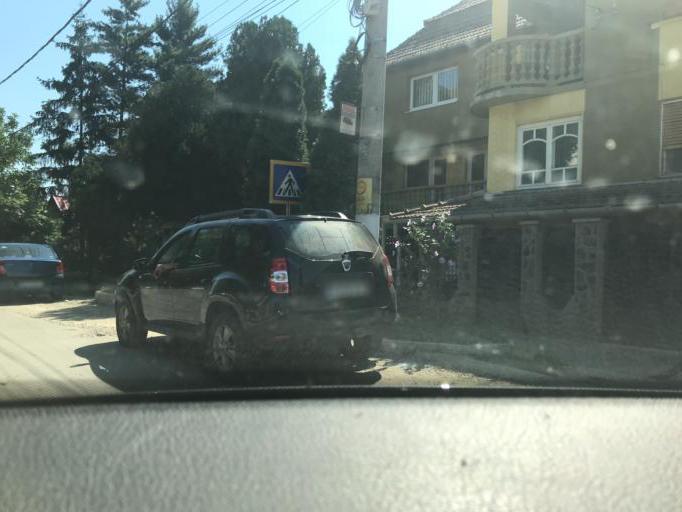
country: RO
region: Bihor
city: Margita
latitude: 47.3420
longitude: 22.3331
